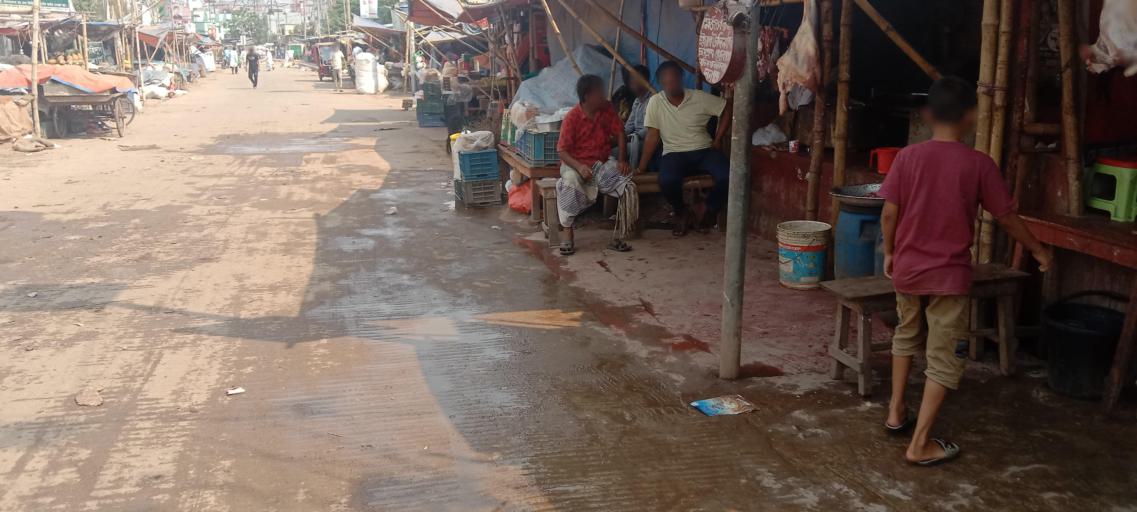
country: BD
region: Dhaka
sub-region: Dhaka
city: Dhaka
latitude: 23.6820
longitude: 90.4247
